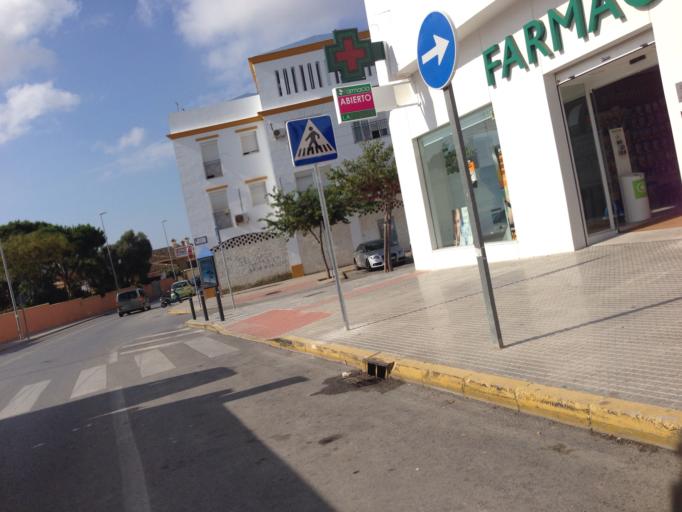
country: ES
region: Andalusia
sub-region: Provincia de Cadiz
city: Chiclana de la Frontera
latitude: 36.4174
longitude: -6.1578
